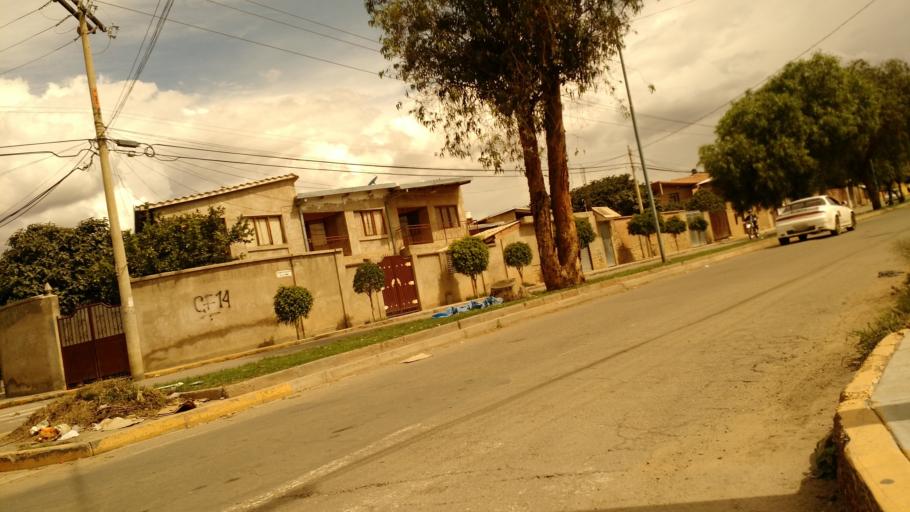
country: BO
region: Cochabamba
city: Cochabamba
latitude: -17.4208
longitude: -66.1236
